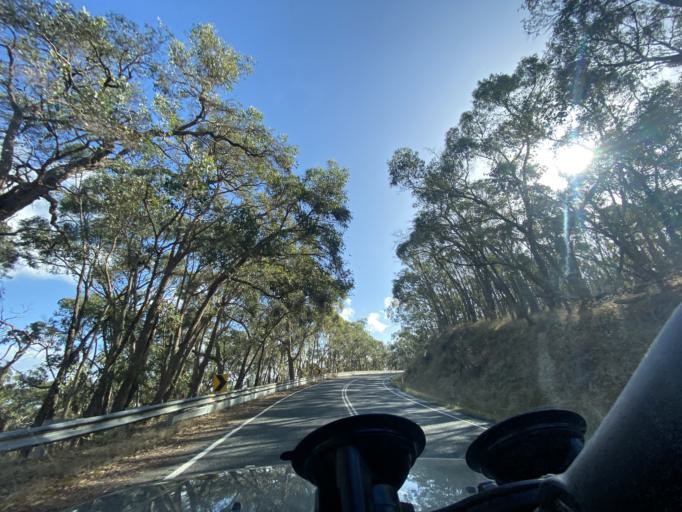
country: AU
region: Victoria
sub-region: Murrindindi
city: Kinglake West
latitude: -37.3019
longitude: 145.3719
